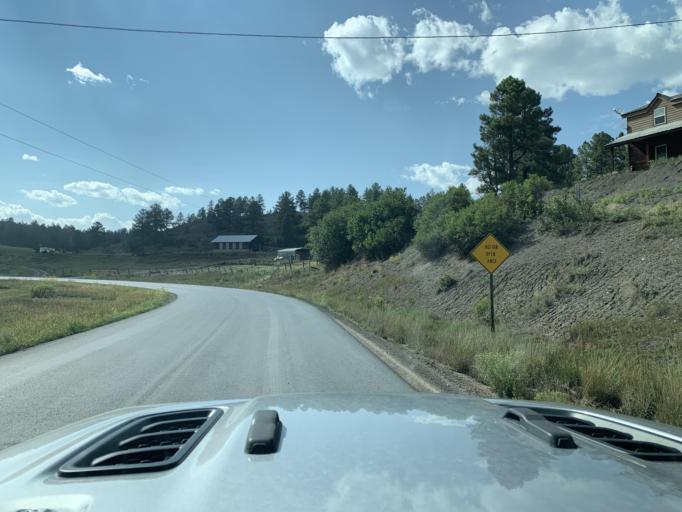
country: US
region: Colorado
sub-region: Archuleta County
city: Pagosa Springs
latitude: 37.2584
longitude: -107.0221
